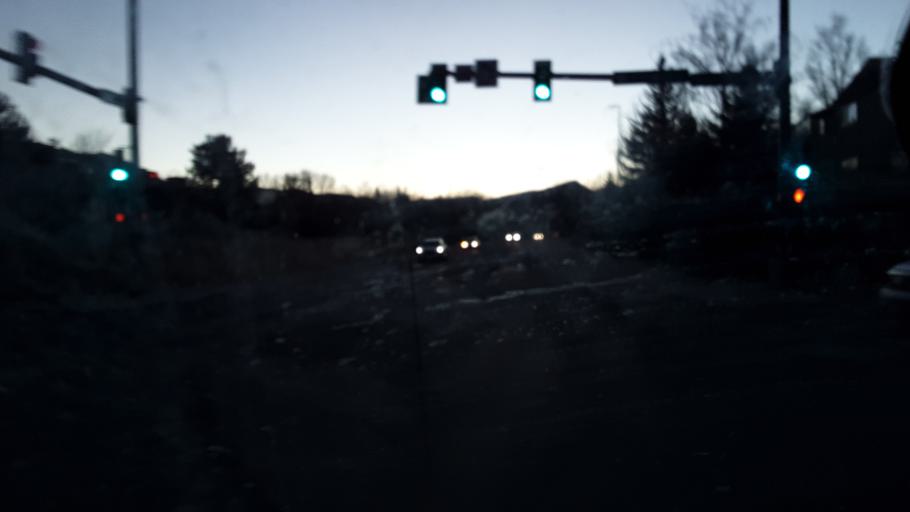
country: US
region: Colorado
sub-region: La Plata County
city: Durango
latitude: 37.2959
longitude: -107.8533
